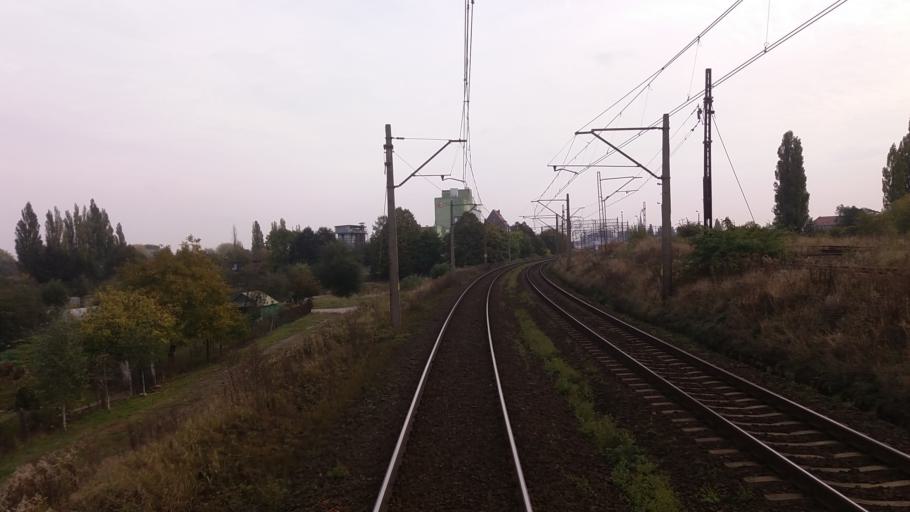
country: PL
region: West Pomeranian Voivodeship
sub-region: Powiat stargardzki
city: Stargard Szczecinski
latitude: 53.3518
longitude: 15.0150
